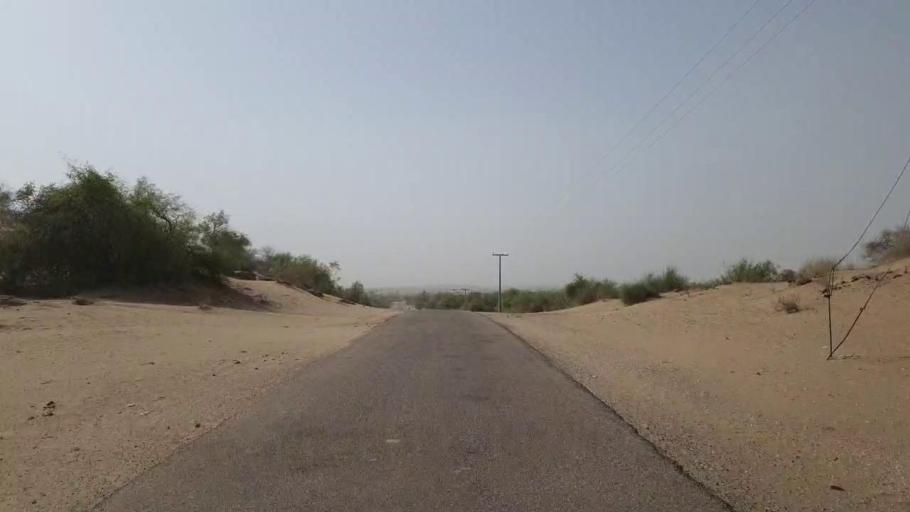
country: PK
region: Sindh
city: Mithi
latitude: 24.5995
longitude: 69.9241
